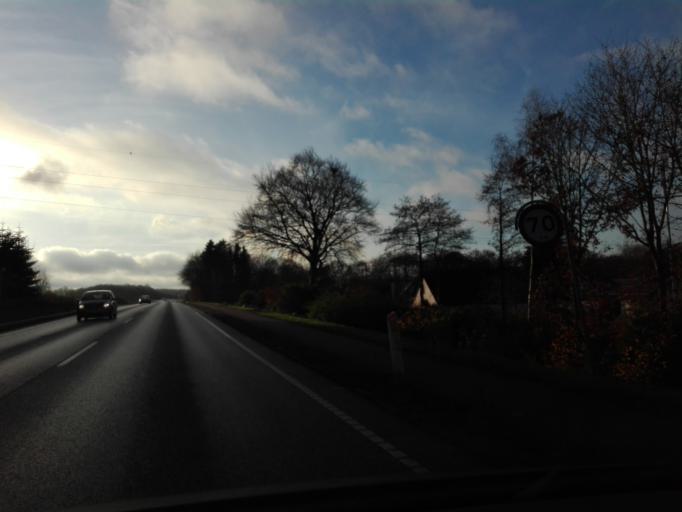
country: DK
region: Central Jutland
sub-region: Skanderborg Kommune
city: Stilling
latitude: 56.0531
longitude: 9.9657
